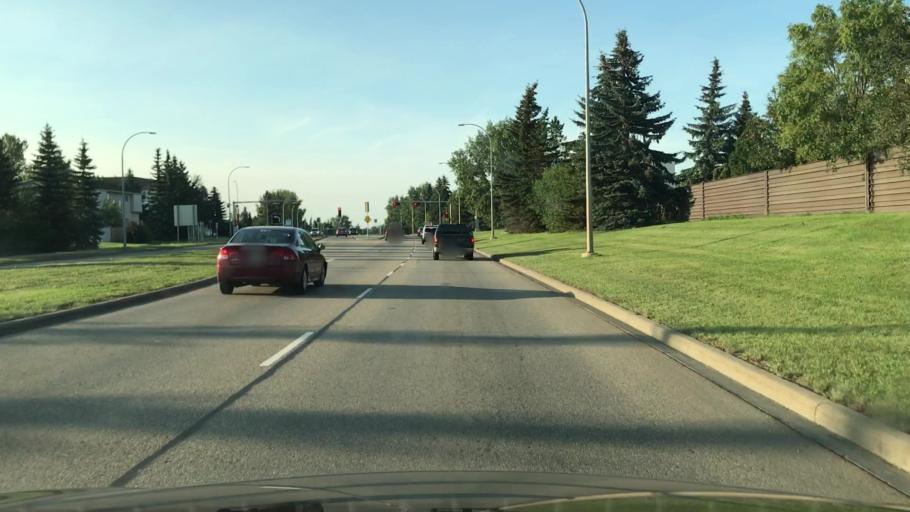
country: CA
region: Alberta
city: Beaumont
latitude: 53.4410
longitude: -113.4184
